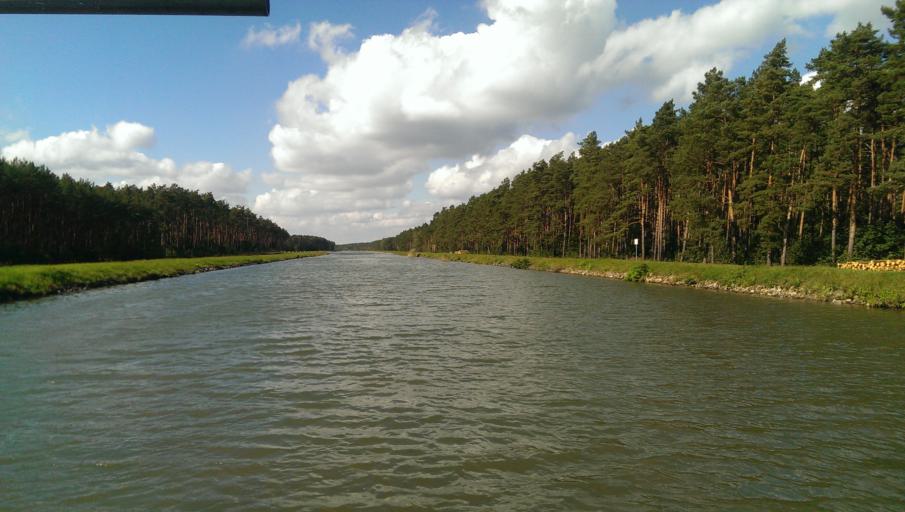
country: DE
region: Brandenburg
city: Niederfinow
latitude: 52.8552
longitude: 13.9023
